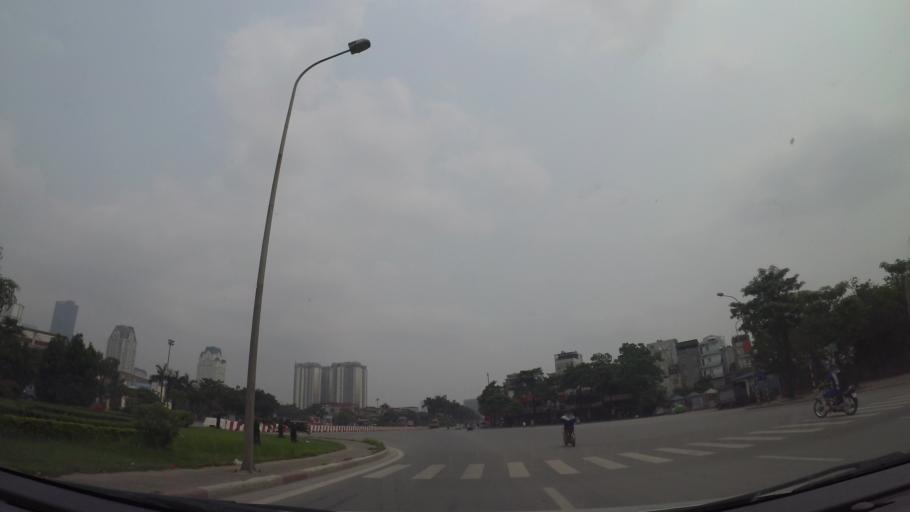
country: VN
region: Ha Noi
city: Cau Dien
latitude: 21.0157
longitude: 105.7679
